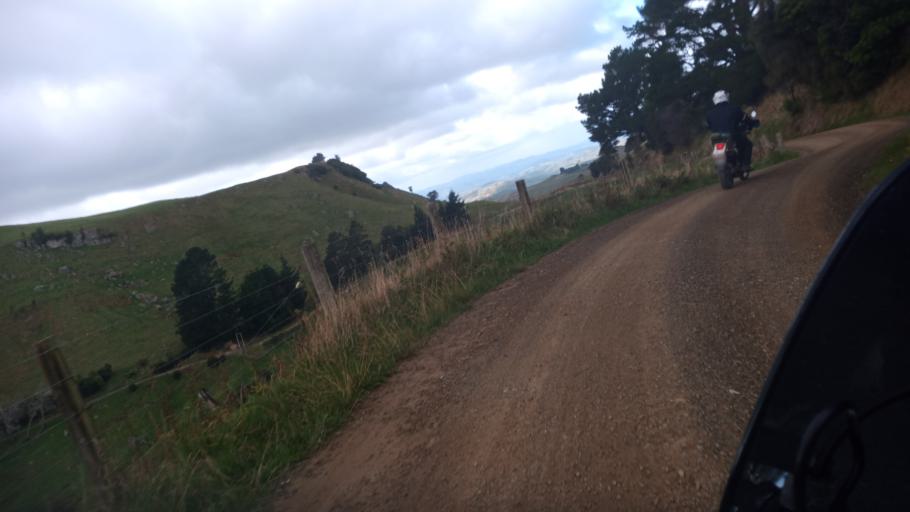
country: NZ
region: Gisborne
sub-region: Gisborne District
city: Gisborne
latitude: -38.4829
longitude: 177.6086
